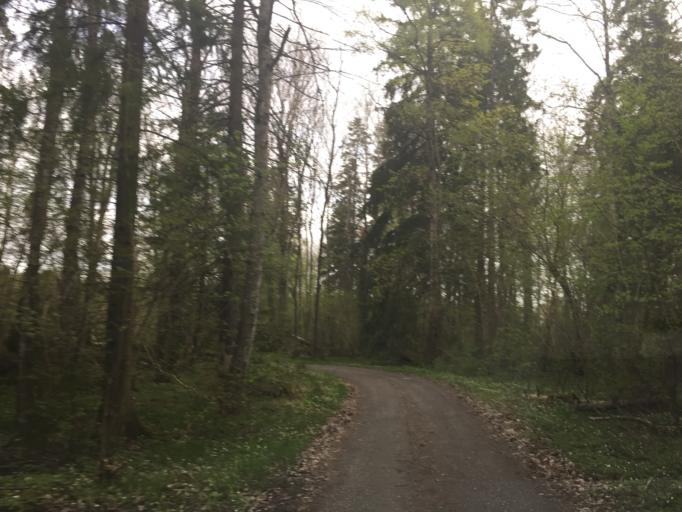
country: SE
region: Vaestmanland
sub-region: Vasteras
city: Tillberga
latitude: 59.6035
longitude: 16.7068
